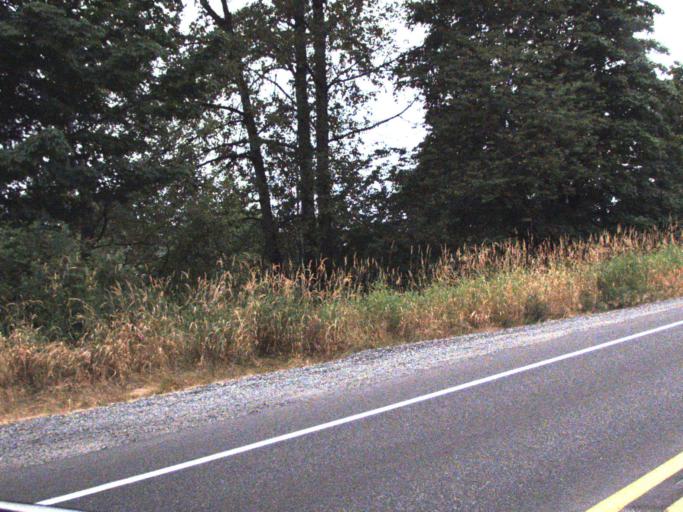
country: US
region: Washington
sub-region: King County
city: Duvall
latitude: 47.7128
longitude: -121.9843
